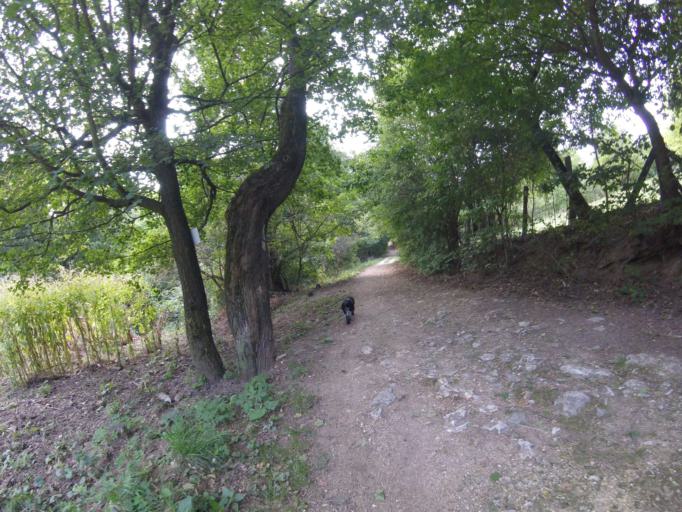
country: HU
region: Pest
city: Pilisszentkereszt
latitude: 47.6946
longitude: 18.9086
